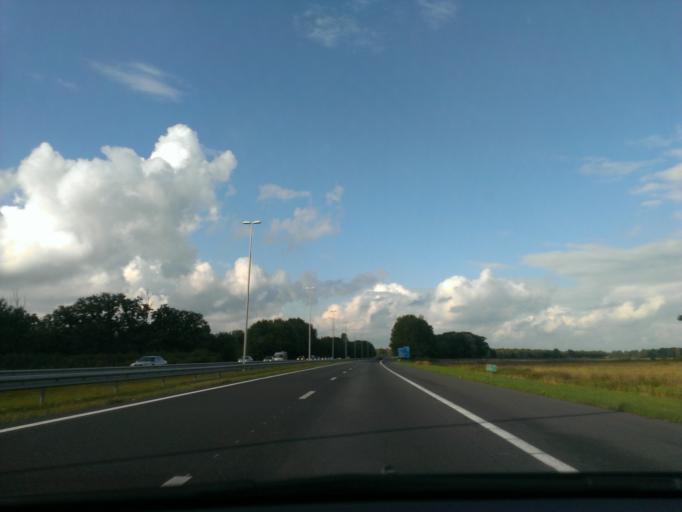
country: NL
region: Gelderland
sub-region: Gemeente Epe
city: Emst
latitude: 52.3201
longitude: 6.0062
